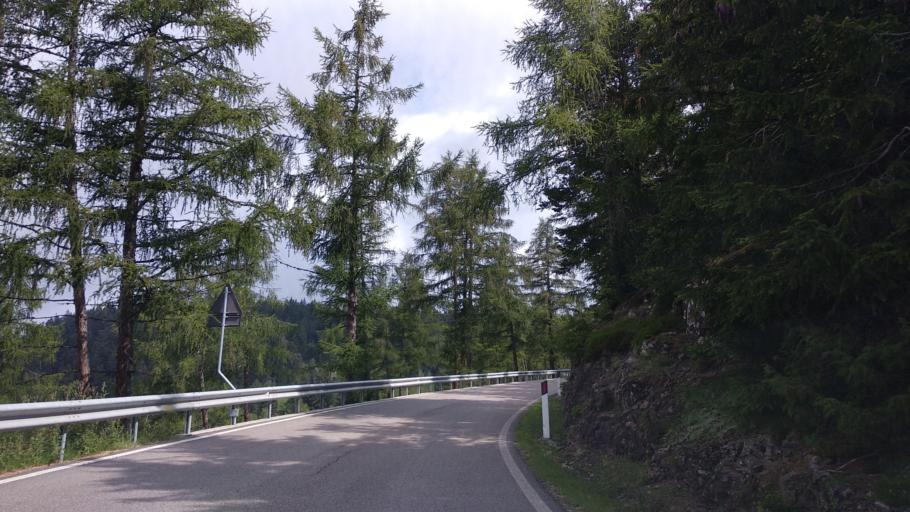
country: IT
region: Trentino-Alto Adige
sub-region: Bolzano
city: Avelengo
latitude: 46.6569
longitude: 11.2291
